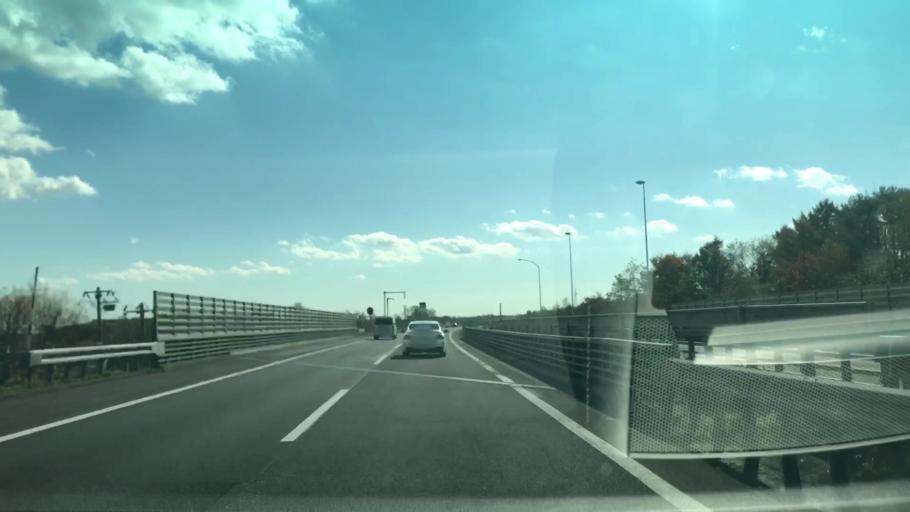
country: JP
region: Hokkaido
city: Kitahiroshima
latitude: 42.9093
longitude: 141.5503
